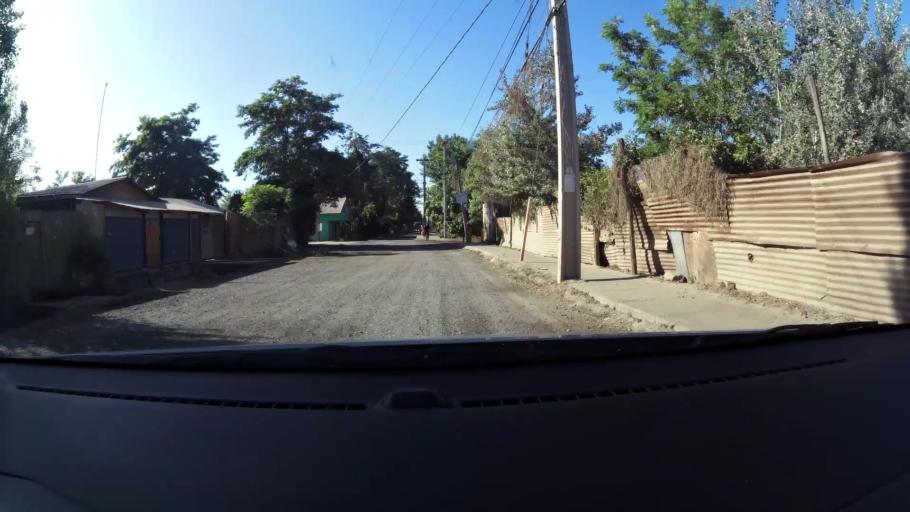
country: CL
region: Santiago Metropolitan
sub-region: Provincia de Maipo
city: San Bernardo
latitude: -33.6428
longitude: -70.6910
